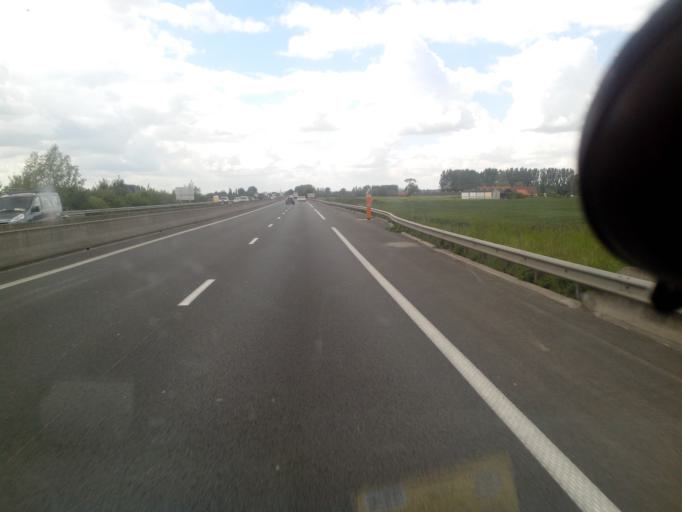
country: FR
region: Nord-Pas-de-Calais
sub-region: Departement du Nord
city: Steenwerck
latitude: 50.7148
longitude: 2.7668
